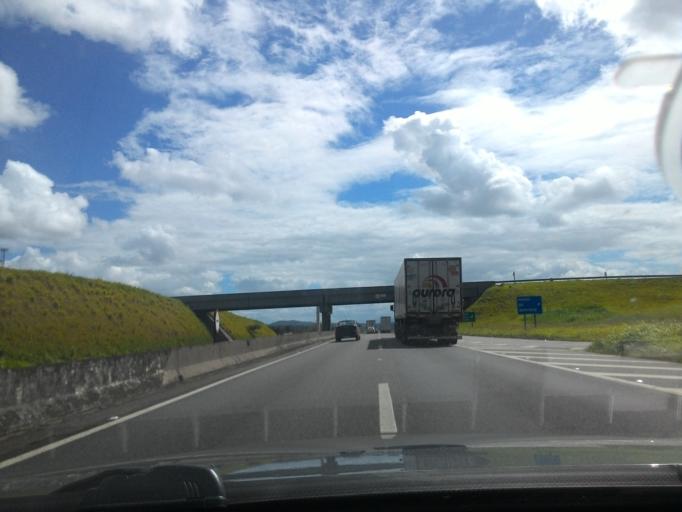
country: BR
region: Sao Paulo
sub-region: Pariquera-Acu
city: Pariquera Acu
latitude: -24.6190
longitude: -47.8920
